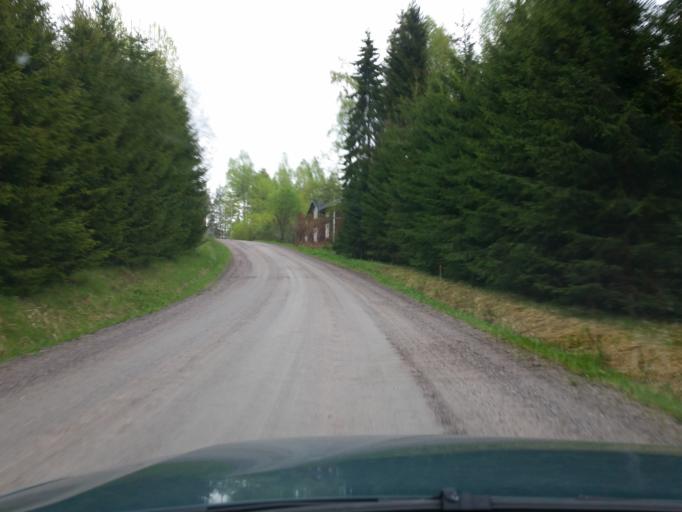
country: FI
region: Uusimaa
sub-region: Helsinki
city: Karjalohja
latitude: 60.1842
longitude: 23.6705
